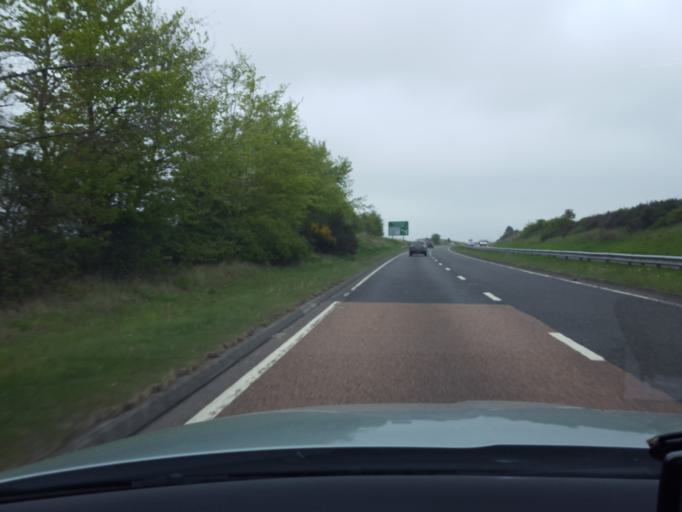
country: GB
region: Scotland
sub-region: Angus
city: Forfar
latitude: 56.6427
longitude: -2.9256
